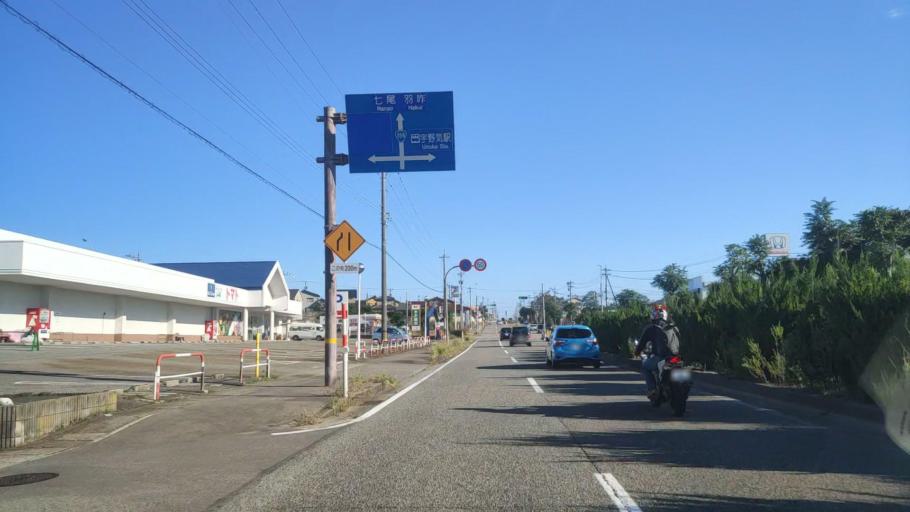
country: JP
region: Ishikawa
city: Tsubata
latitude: 36.7216
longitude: 136.6982
